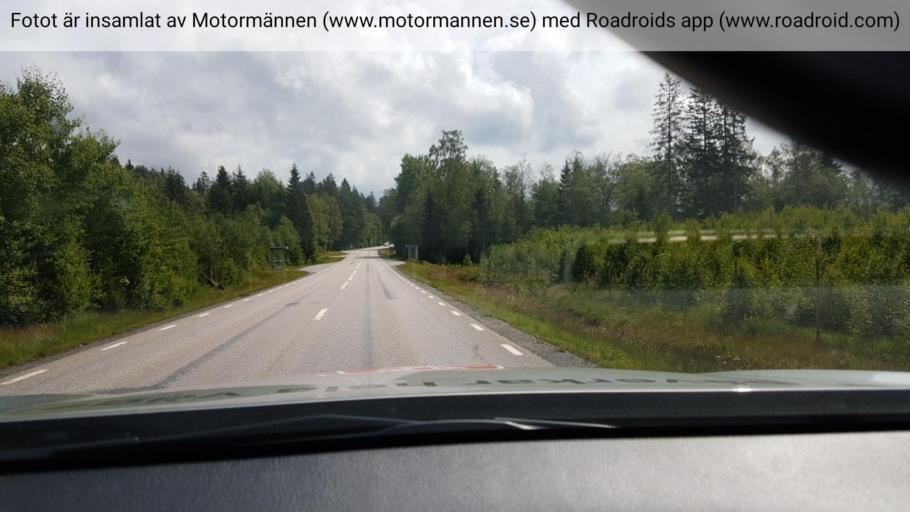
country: SE
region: Vaestra Goetaland
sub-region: Svenljunga Kommun
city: Svenljunga
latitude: 57.4885
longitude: 12.9929
